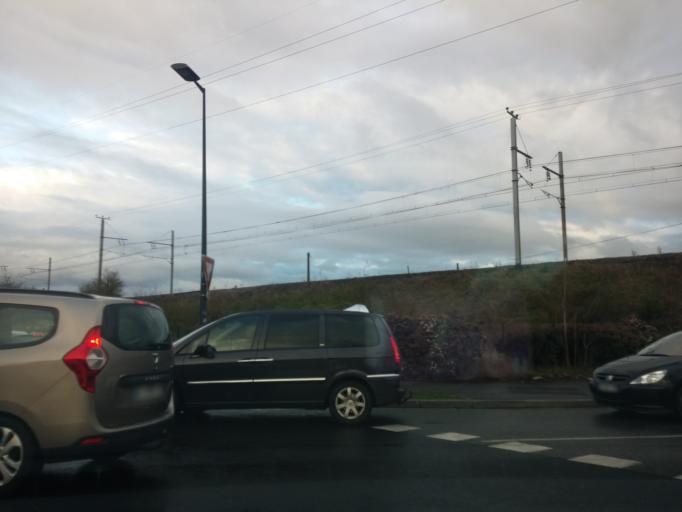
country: FR
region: Midi-Pyrenees
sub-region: Departement de la Haute-Garonne
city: Toulouse
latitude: 43.5690
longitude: 1.4245
